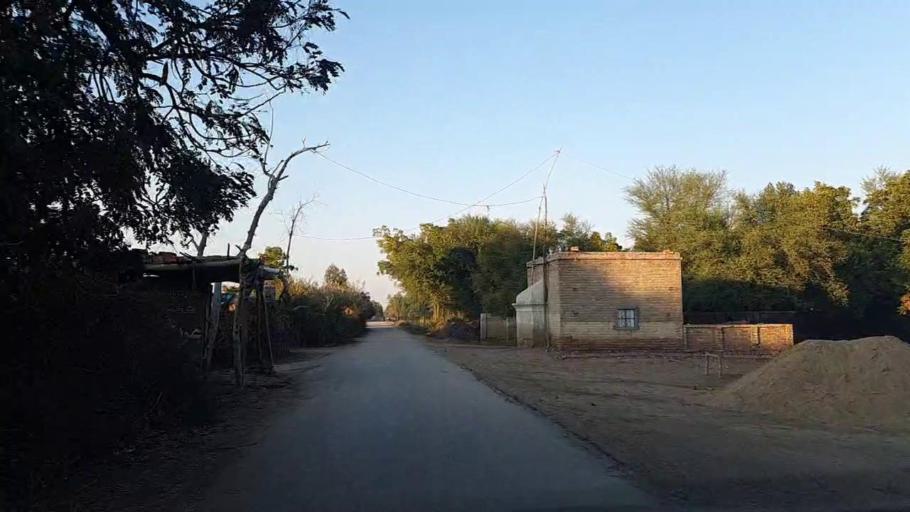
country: PK
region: Sindh
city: Nawabshah
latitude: 26.2407
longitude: 68.3383
